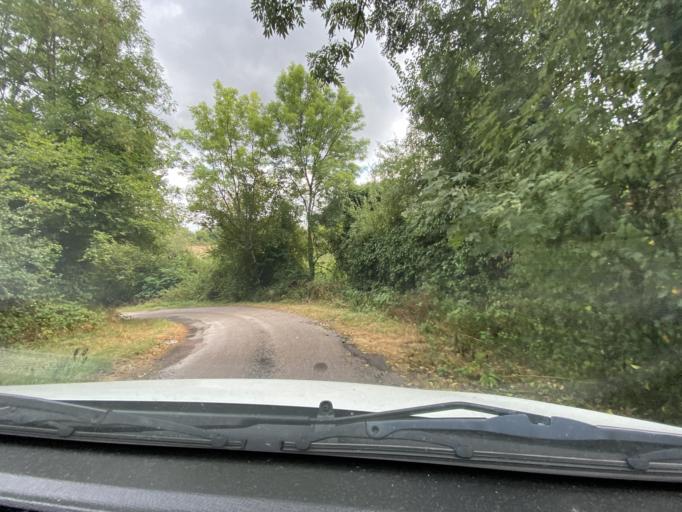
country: FR
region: Bourgogne
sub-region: Departement de la Cote-d'Or
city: Saulieu
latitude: 47.2797
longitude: 4.2396
